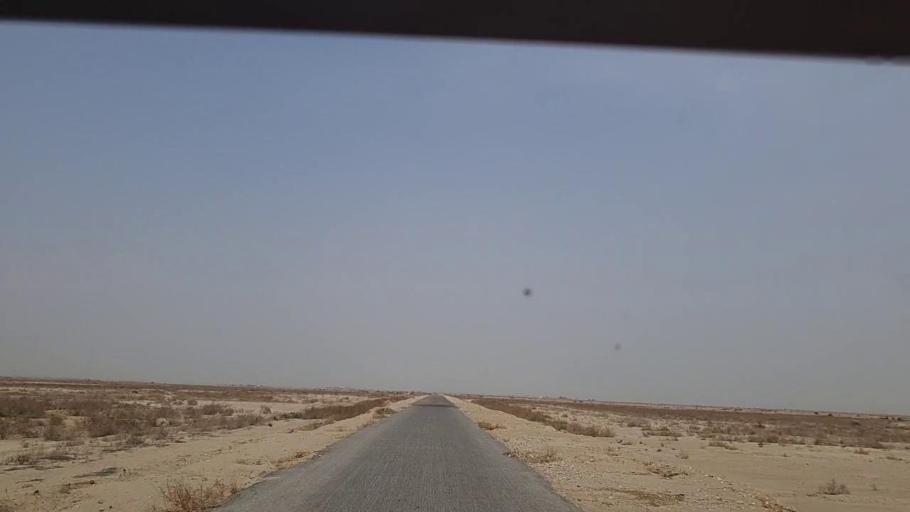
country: PK
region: Sindh
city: Phulji
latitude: 27.0051
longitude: 67.5357
